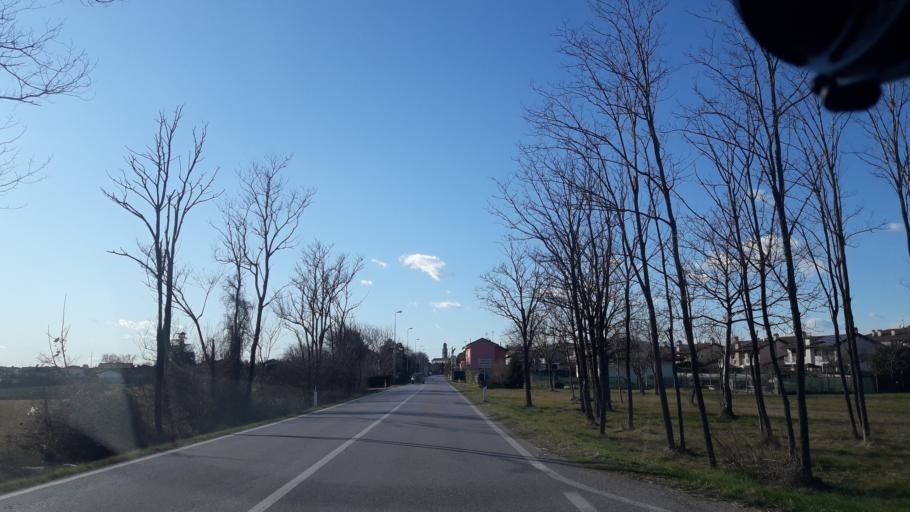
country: IT
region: Friuli Venezia Giulia
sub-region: Provincia di Udine
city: Campoformido
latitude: 46.0203
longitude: 13.1703
